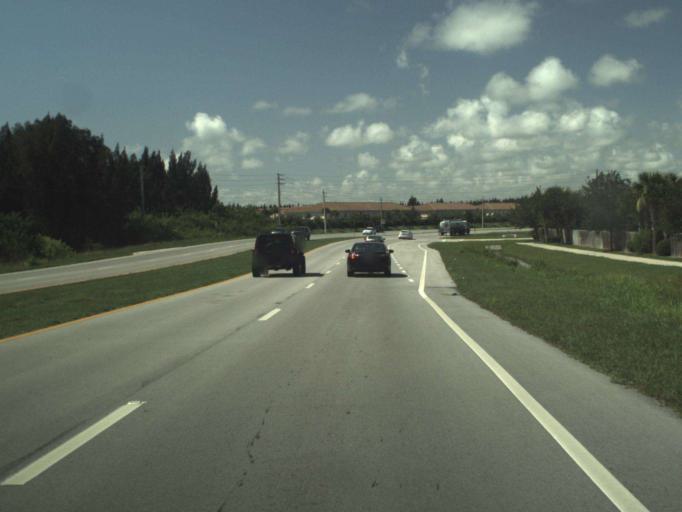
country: US
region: Florida
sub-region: Indian River County
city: Vero Beach
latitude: 27.6265
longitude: -80.3787
